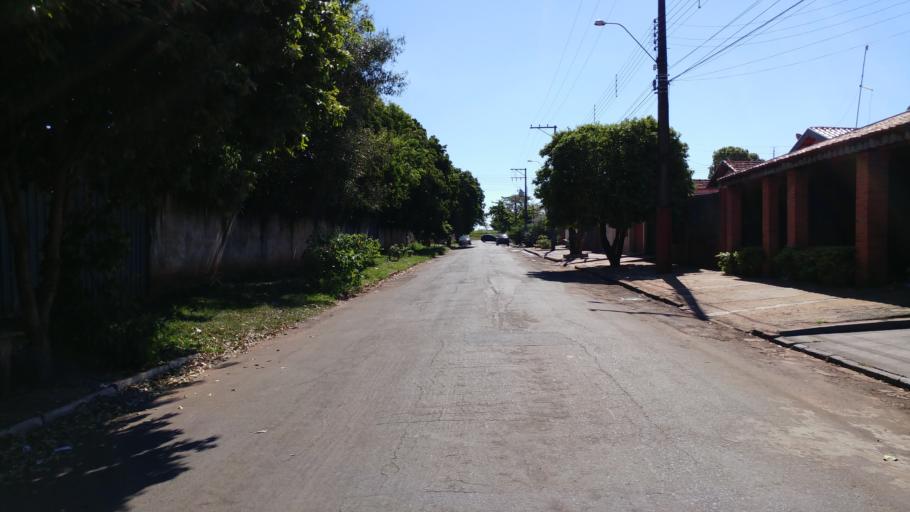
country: BR
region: Sao Paulo
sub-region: Paraguacu Paulista
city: Paraguacu Paulista
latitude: -22.4346
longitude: -50.5853
